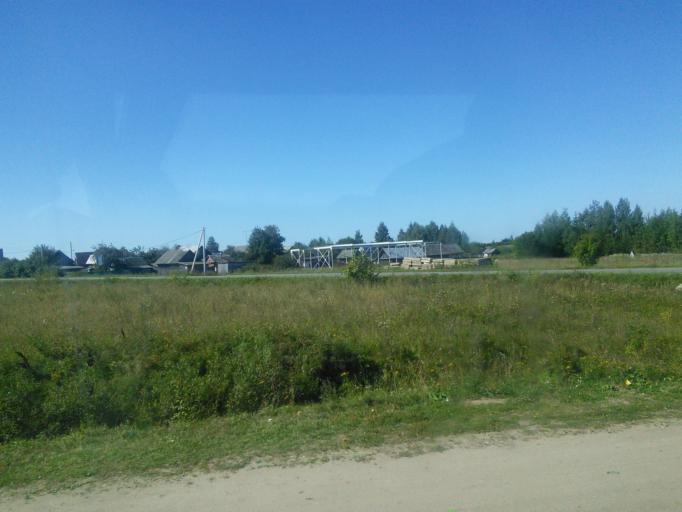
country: RU
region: Tverskaya
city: Kalyazin
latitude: 57.2133
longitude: 37.8698
